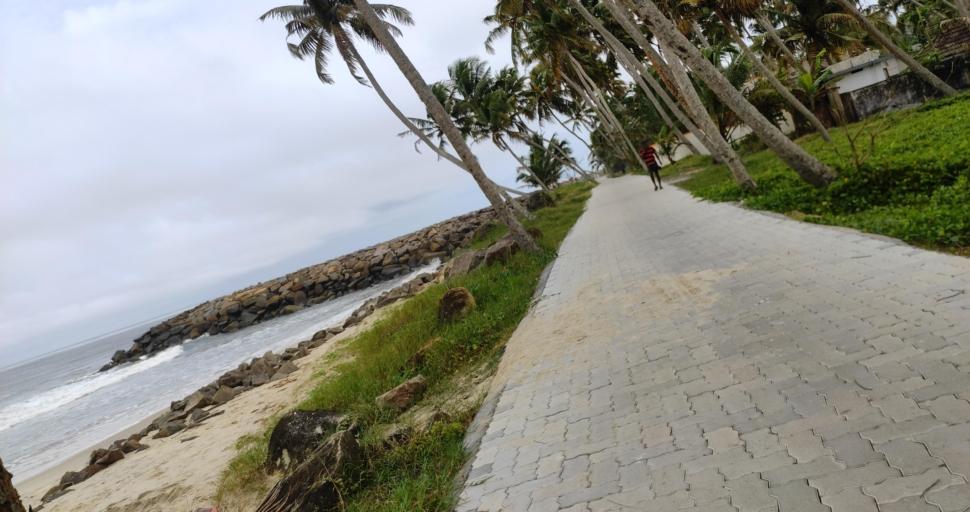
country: IN
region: Kerala
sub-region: Alappuzha
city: Vayalar
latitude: 9.6769
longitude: 76.2912
